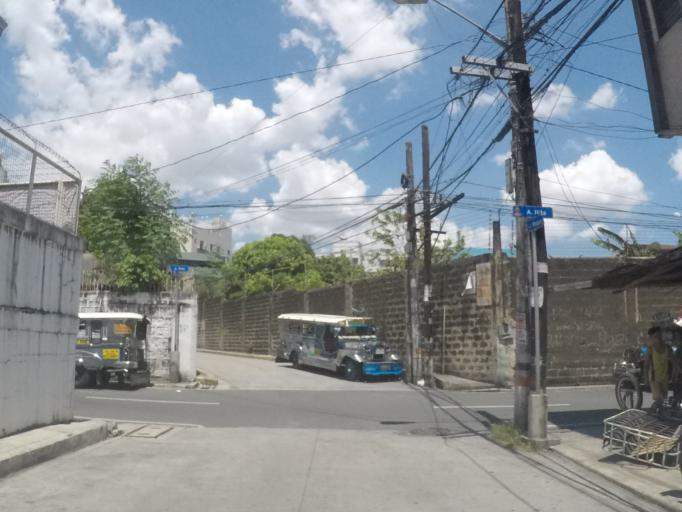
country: PH
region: Metro Manila
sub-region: San Juan
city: San Juan
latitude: 14.5995
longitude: 121.0260
